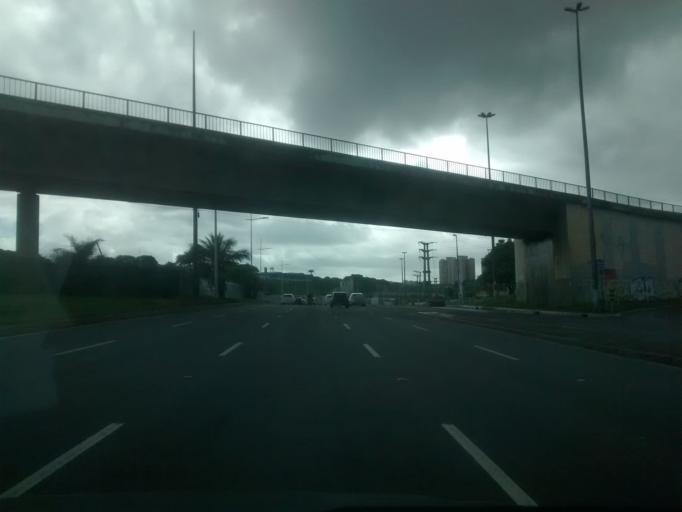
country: BR
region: Bahia
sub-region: Salvador
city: Salvador
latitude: -12.9434
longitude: -38.4195
